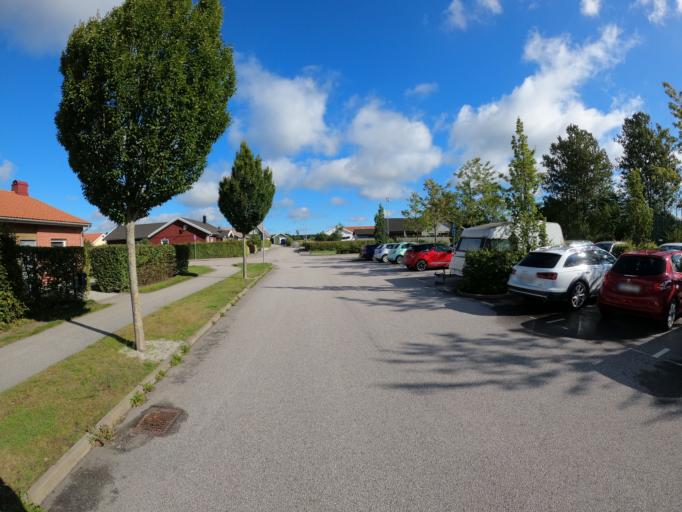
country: SE
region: Skane
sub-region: Lunds Kommun
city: Genarp
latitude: 55.6027
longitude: 13.4064
